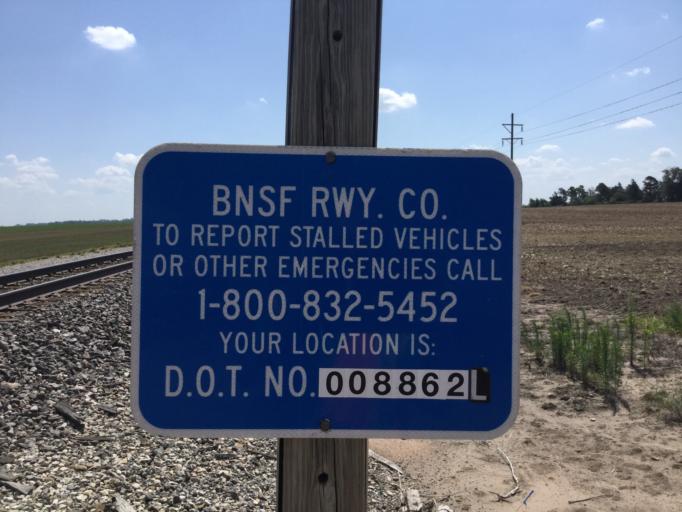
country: US
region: Kansas
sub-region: Harvey County
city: Halstead
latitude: 38.0161
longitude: -97.6104
